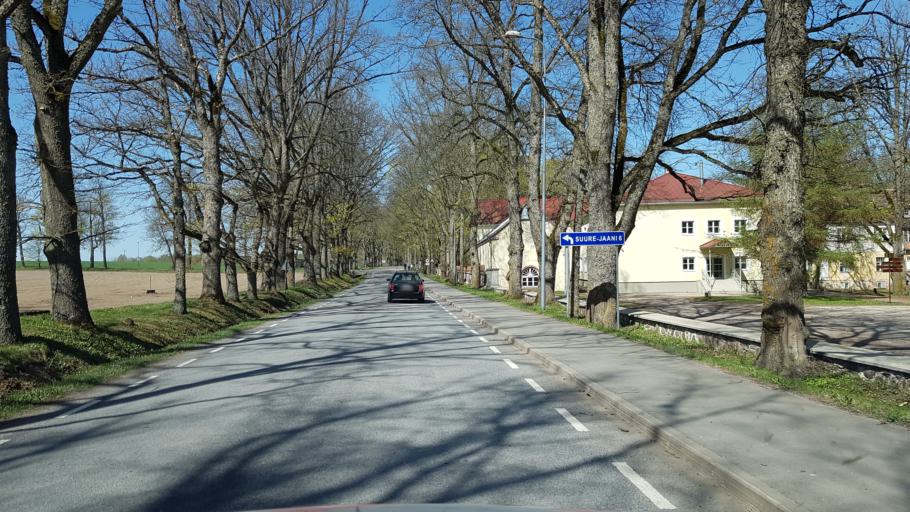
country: EE
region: Viljandimaa
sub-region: Vohma linn
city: Vohma
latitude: 58.5527
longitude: 25.5645
